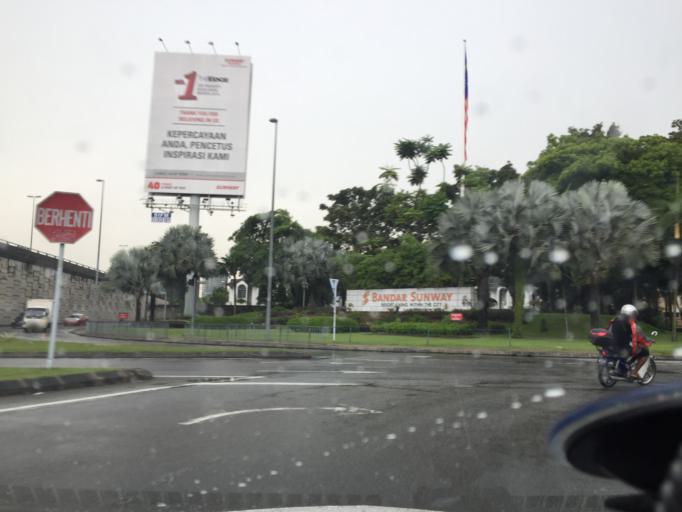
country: MY
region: Selangor
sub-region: Petaling
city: Petaling Jaya
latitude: 3.0746
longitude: 101.6133
